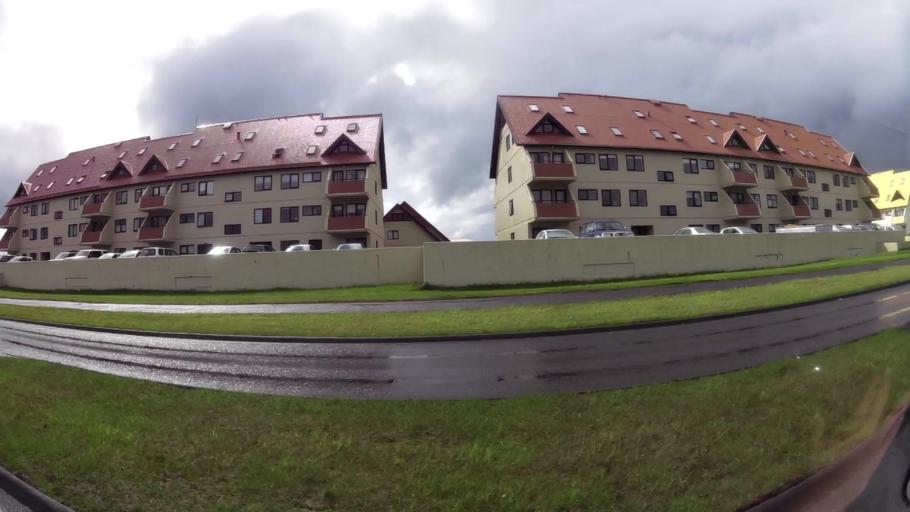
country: IS
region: Capital Region
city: Seltjarnarnes
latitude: 64.1497
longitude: -21.9727
